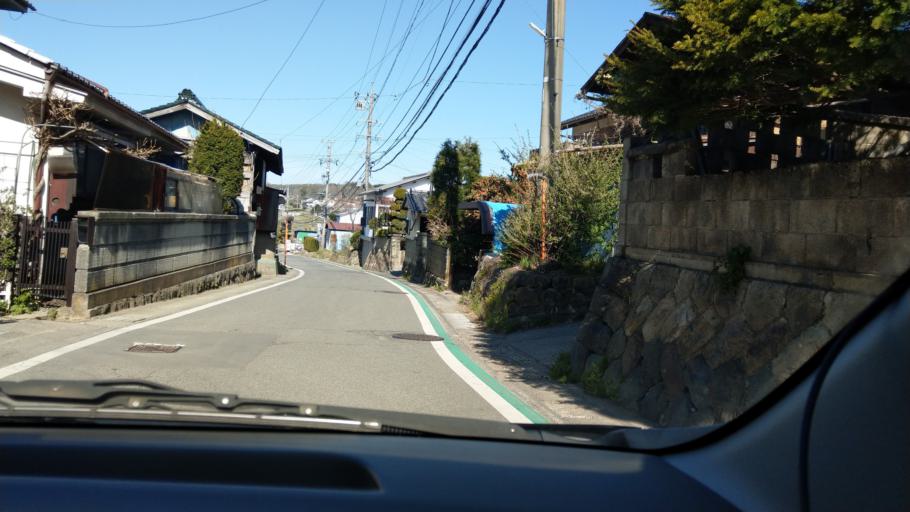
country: JP
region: Nagano
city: Komoro
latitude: 36.3353
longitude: 138.4910
